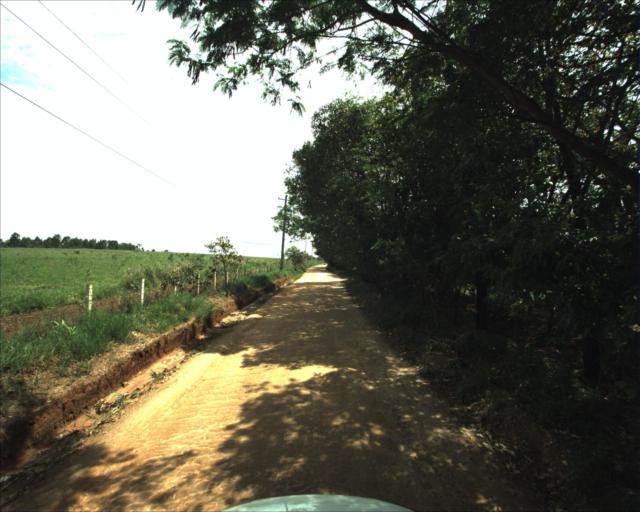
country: BR
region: Sao Paulo
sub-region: Aracoiaba Da Serra
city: Aracoiaba da Serra
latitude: -23.5528
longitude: -47.5466
